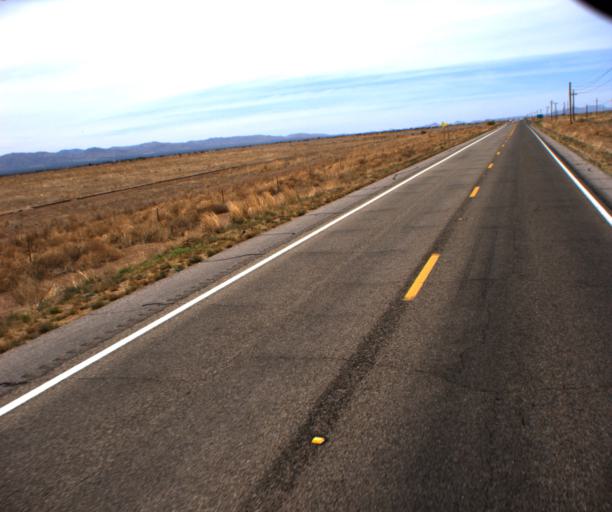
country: US
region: Arizona
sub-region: Cochise County
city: Pirtleville
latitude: 31.4429
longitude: -109.5975
